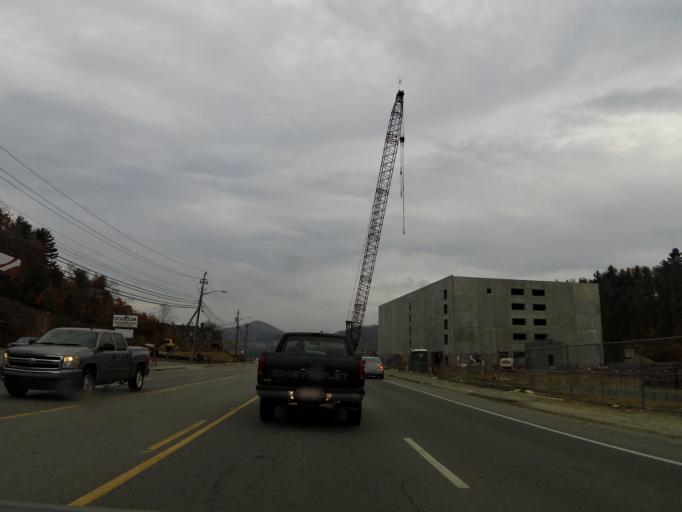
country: US
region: North Carolina
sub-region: Watauga County
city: Boone
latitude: 36.2080
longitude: -81.6724
